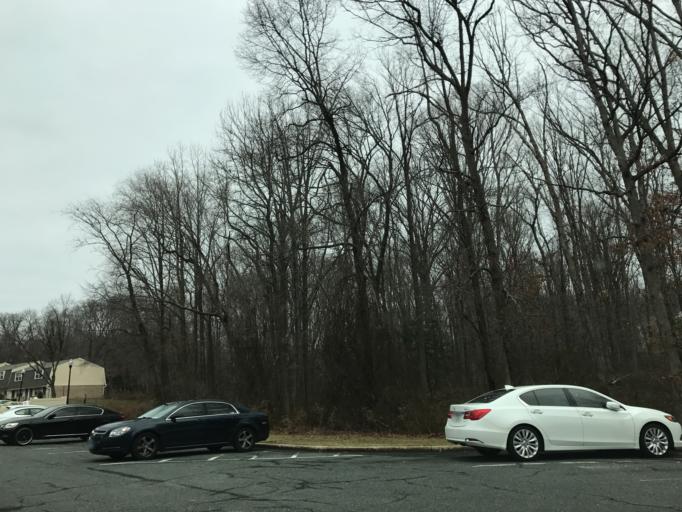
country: US
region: Maryland
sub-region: Baltimore County
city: Rossville
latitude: 39.3480
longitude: -76.4831
